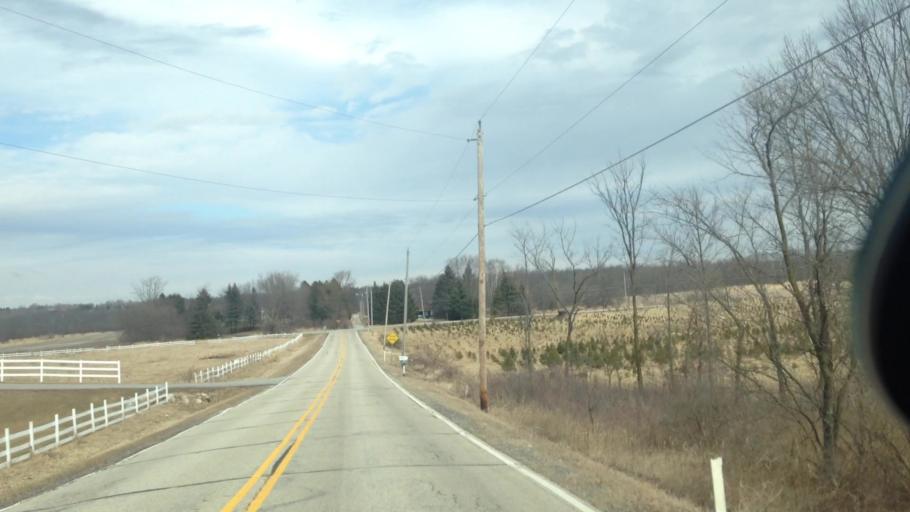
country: US
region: Wisconsin
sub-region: Waukesha County
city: Sussex
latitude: 43.1605
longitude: -88.2233
